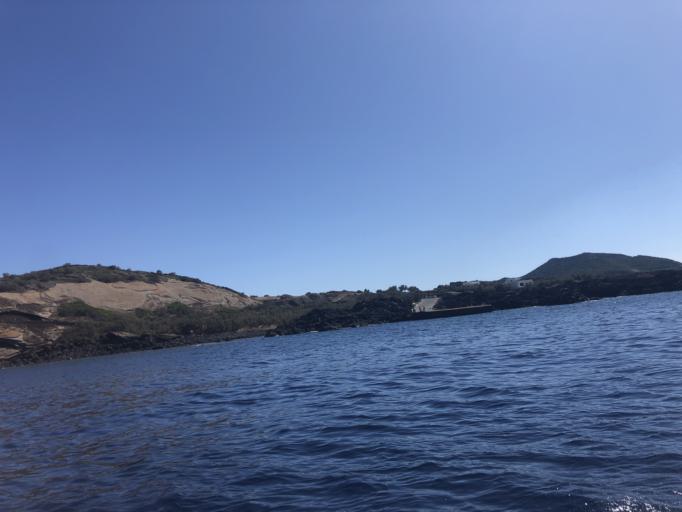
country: IT
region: Sicily
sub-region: Agrigento
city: Lampedusa
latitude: 35.8764
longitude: 12.8657
